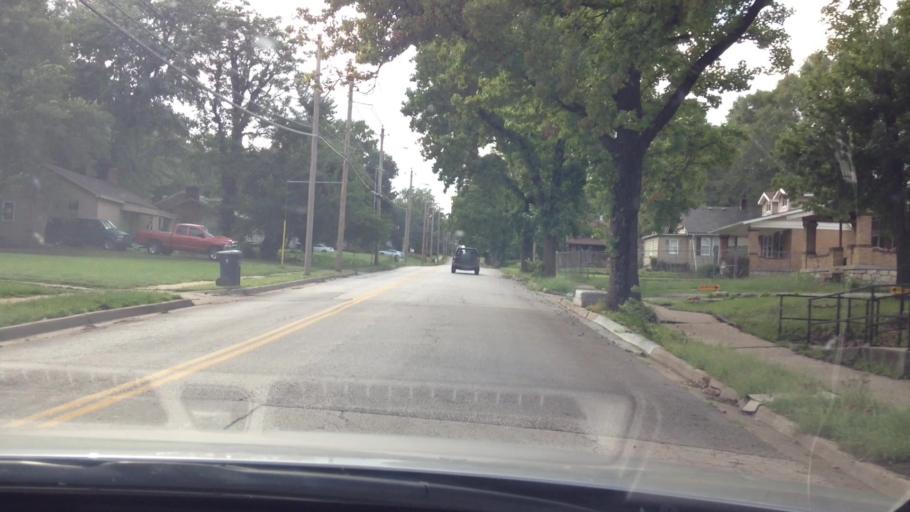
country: US
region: Kansas
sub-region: Johnson County
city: Mission Hills
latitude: 39.0195
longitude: -94.5614
